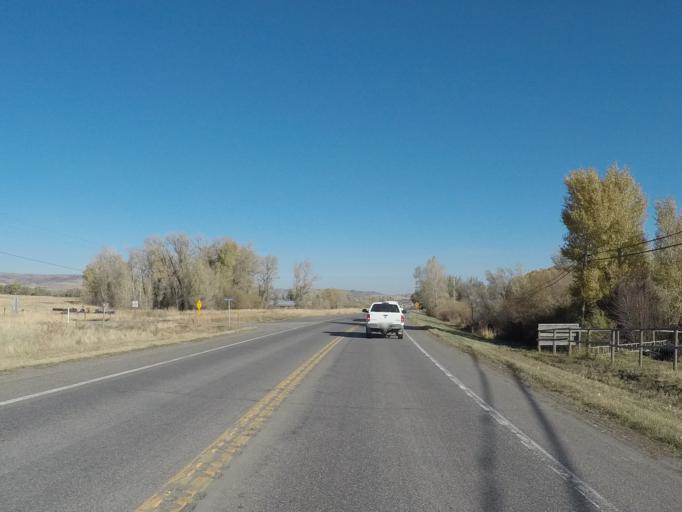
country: US
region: Montana
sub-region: Park County
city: Livingston
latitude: 45.6194
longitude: -110.5790
